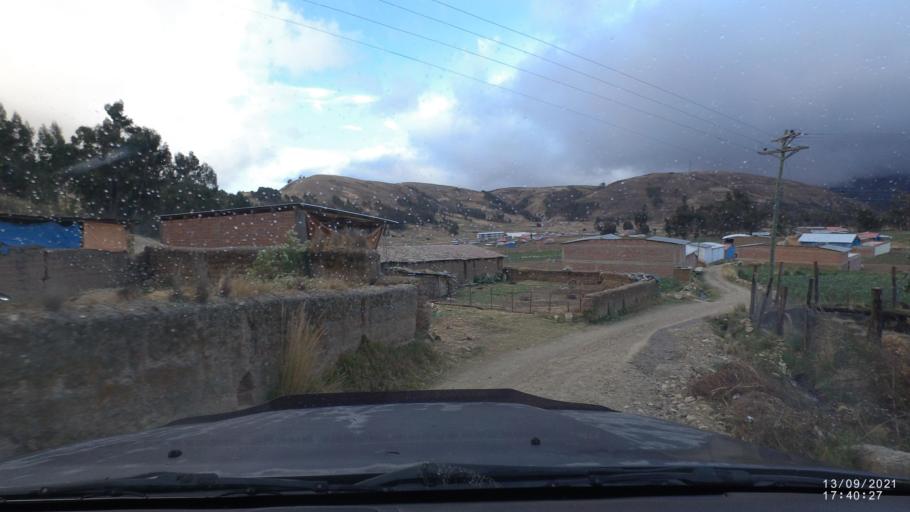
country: BO
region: Cochabamba
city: Colomi
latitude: -17.3628
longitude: -65.8099
